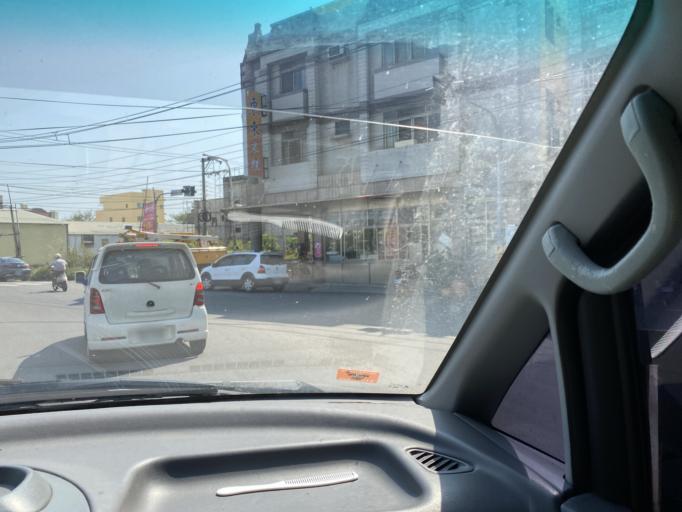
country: TW
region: Taiwan
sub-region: Changhua
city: Chang-hua
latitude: 23.9034
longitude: 120.3644
